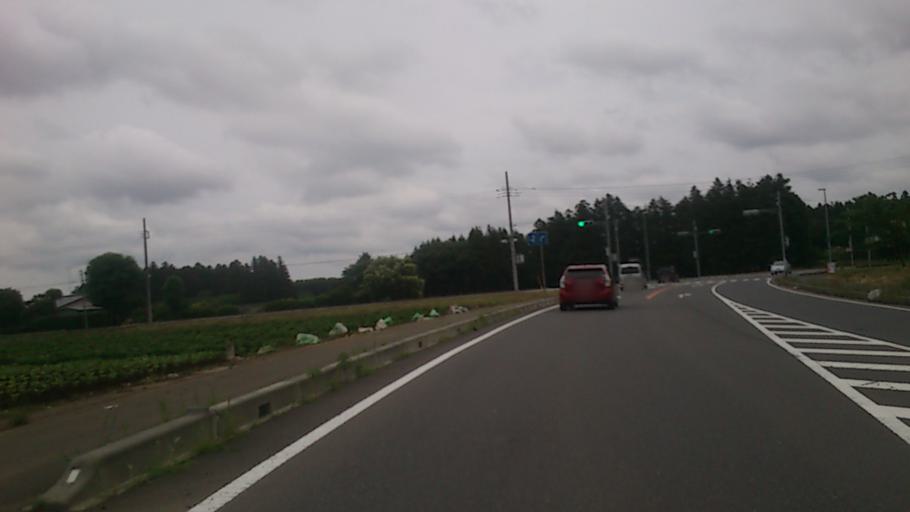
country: JP
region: Ibaraki
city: Ishioka
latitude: 36.2346
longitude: 140.3227
